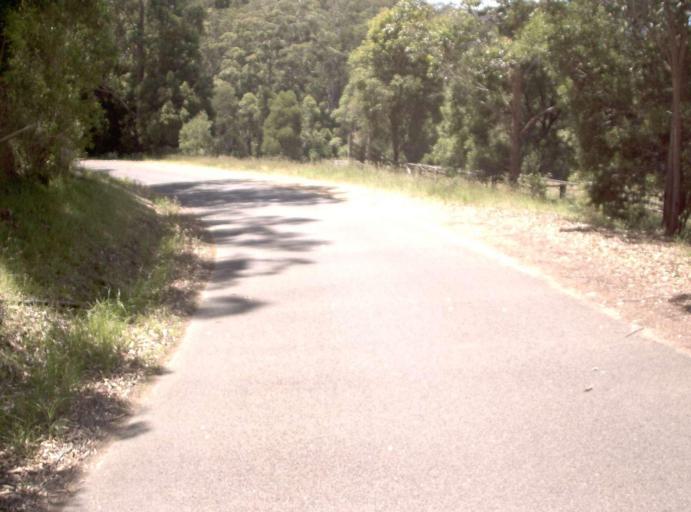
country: AU
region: New South Wales
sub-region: Bombala
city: Bombala
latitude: -37.4635
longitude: 148.9384
